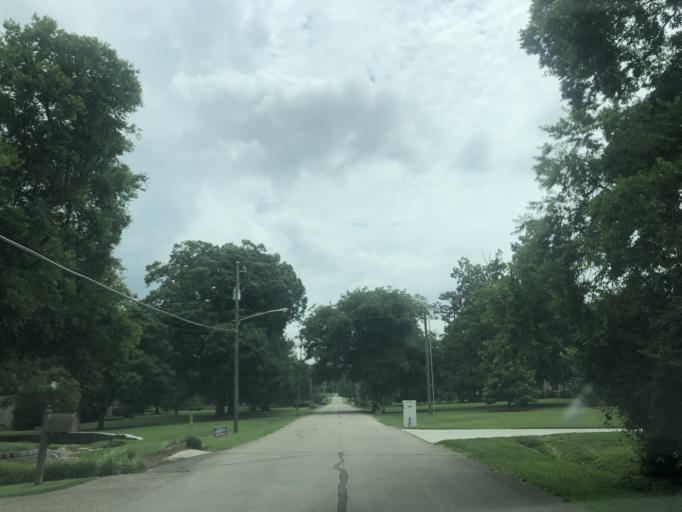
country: US
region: Tennessee
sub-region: Davidson County
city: Oak Hill
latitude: 36.0851
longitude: -86.7877
